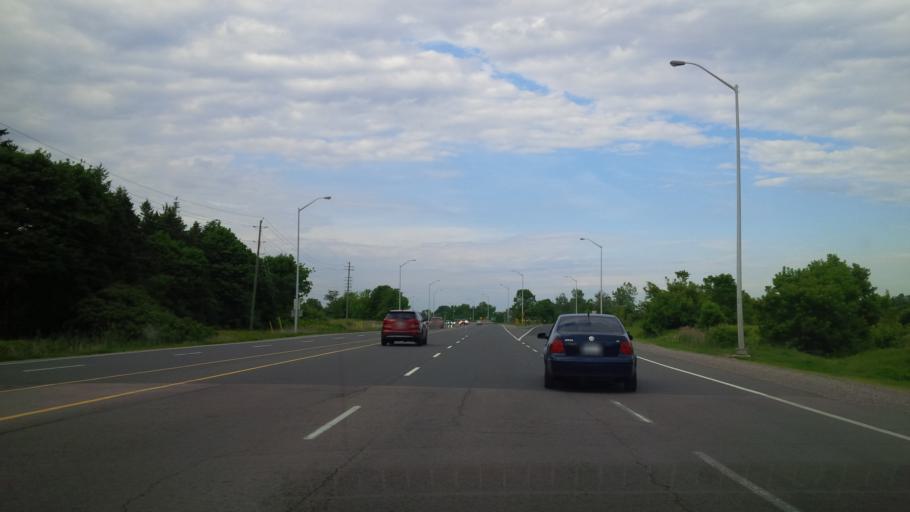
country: CA
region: Ontario
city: Ancaster
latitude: 43.2027
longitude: -80.0109
